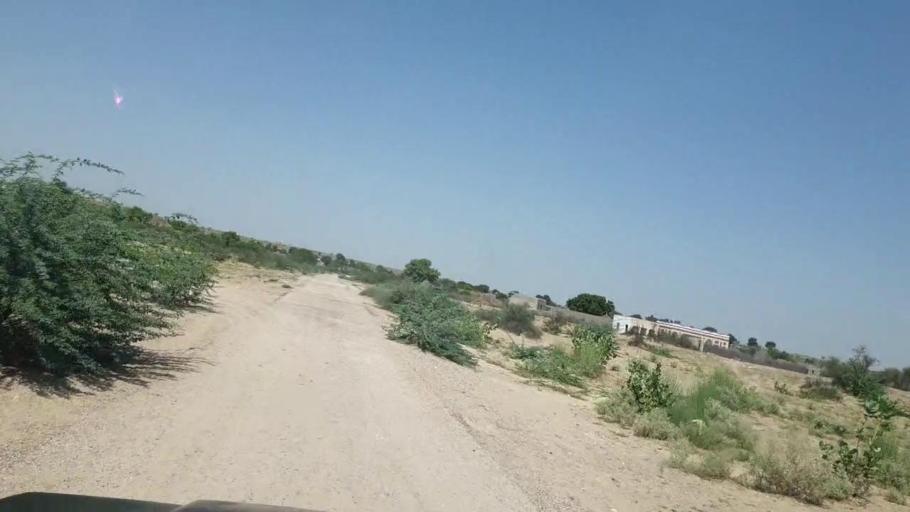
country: PK
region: Sindh
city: Chor
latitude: 25.3726
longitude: 70.3174
